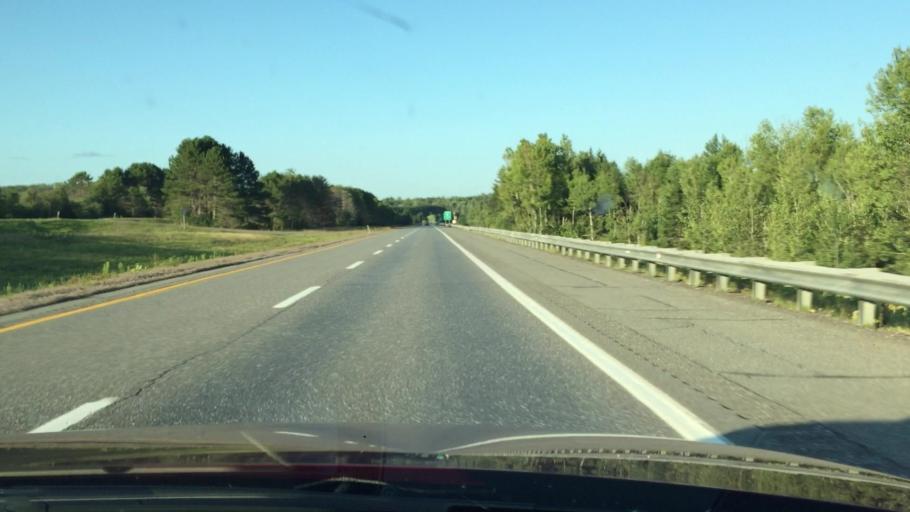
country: US
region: Maine
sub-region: Aroostook County
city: Hodgdon
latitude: 46.1407
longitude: -68.0696
